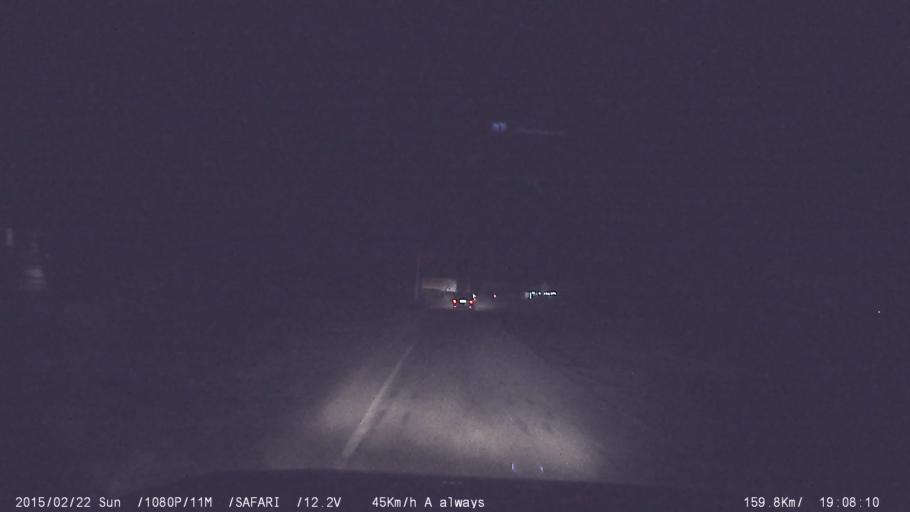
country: IN
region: Tamil Nadu
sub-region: Theni
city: Teni
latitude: 10.0497
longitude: 77.5019
